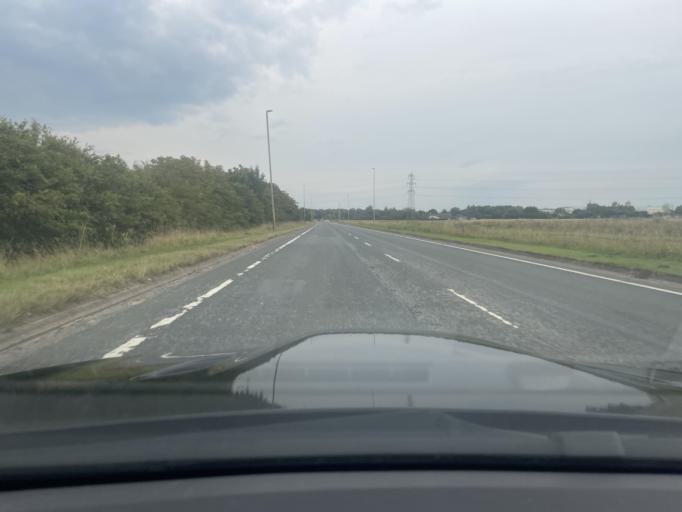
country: GB
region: England
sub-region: Lancashire
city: Leyland
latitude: 53.7091
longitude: -2.7164
